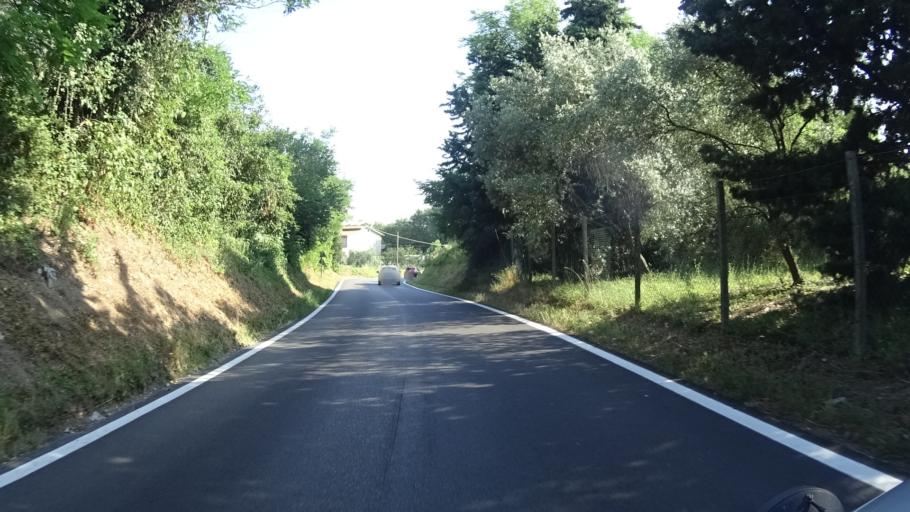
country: IT
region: Veneto
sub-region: Provincia di Verona
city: Calmasino
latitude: 45.5075
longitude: 10.7560
